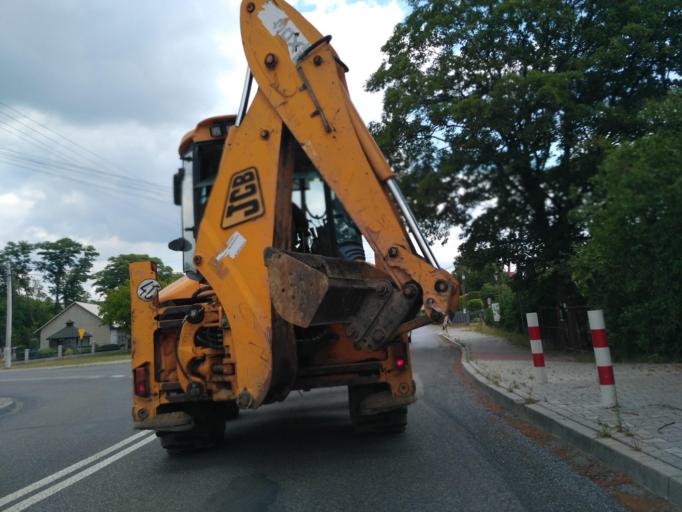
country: PL
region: Subcarpathian Voivodeship
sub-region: Powiat debicki
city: Zyrakow
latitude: 50.0483
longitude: 21.3416
